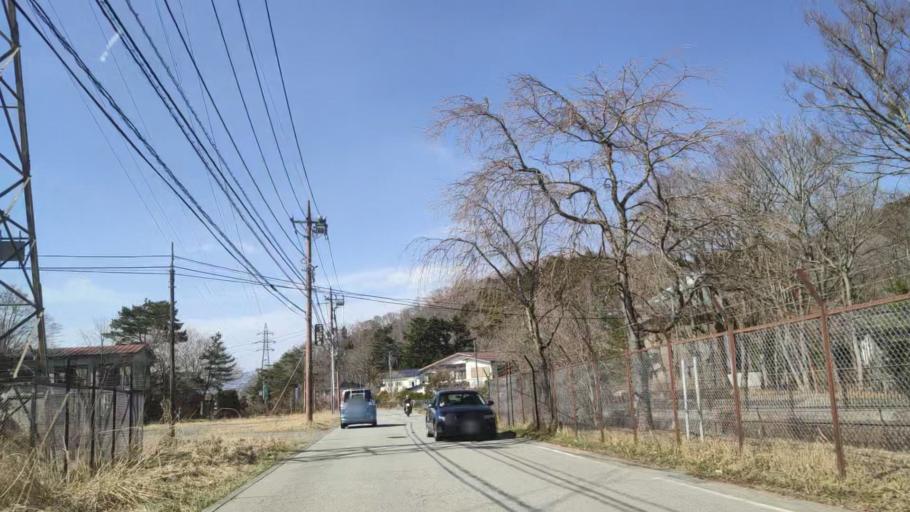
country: JP
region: Shizuoka
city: Gotemba
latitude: 35.4298
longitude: 138.8515
